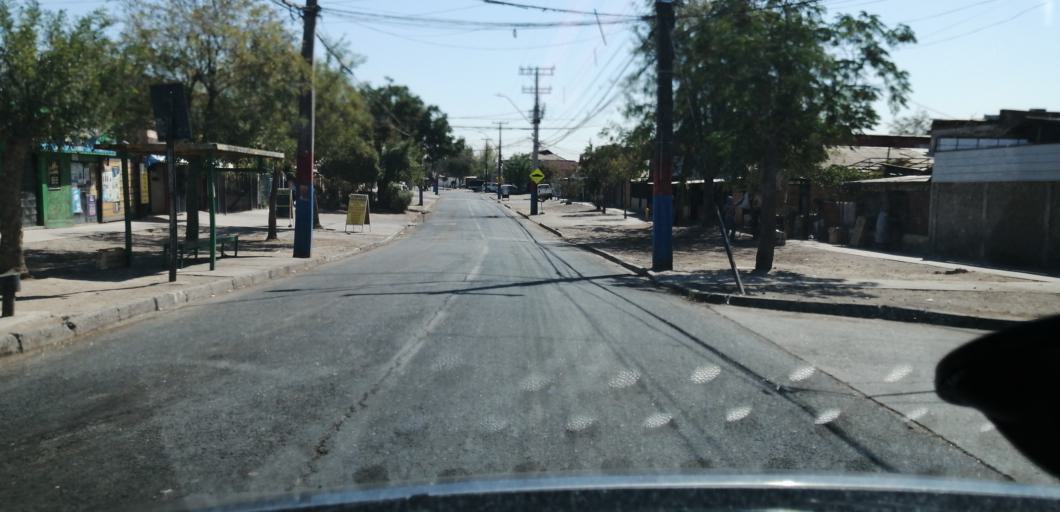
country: CL
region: Santiago Metropolitan
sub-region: Provincia de Santiago
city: Lo Prado
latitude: -33.4407
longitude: -70.7580
